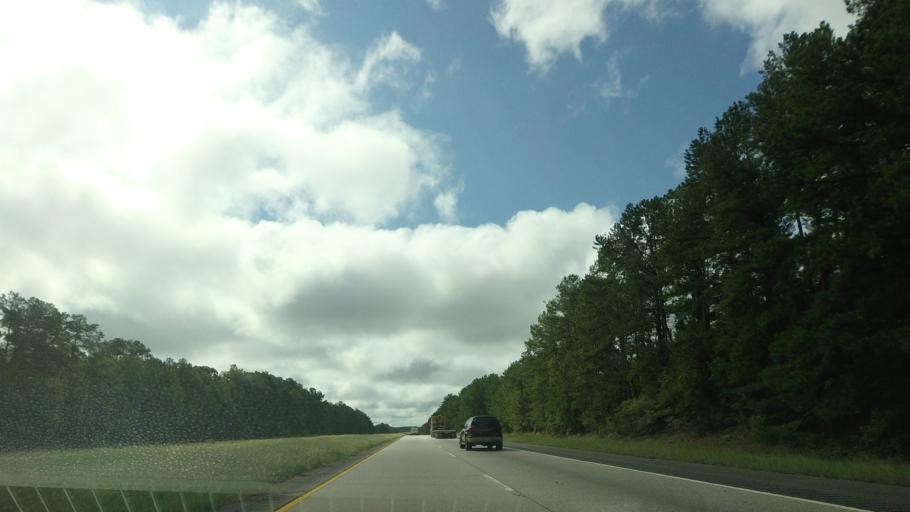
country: US
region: Georgia
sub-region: Houston County
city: Warner Robins
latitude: 32.7347
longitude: -83.5402
